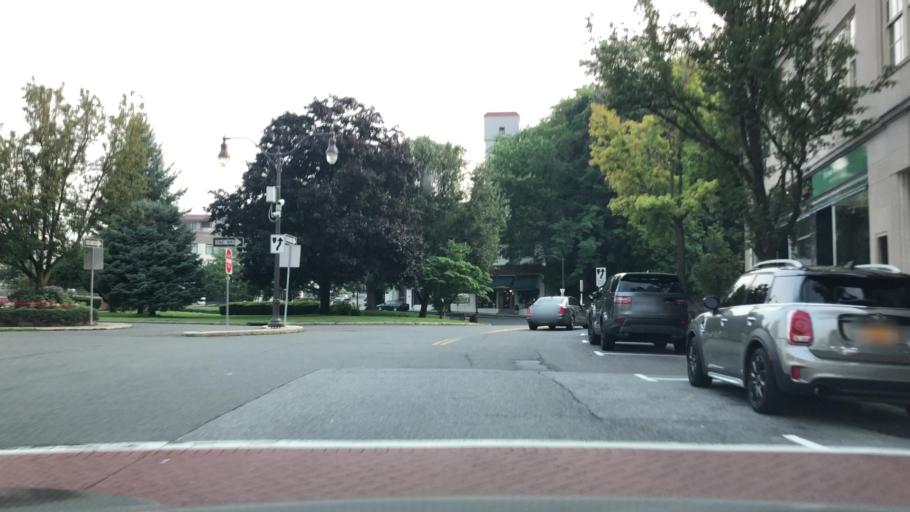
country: US
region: New York
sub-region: Westchester County
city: Bronxville
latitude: 40.9408
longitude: -73.8344
